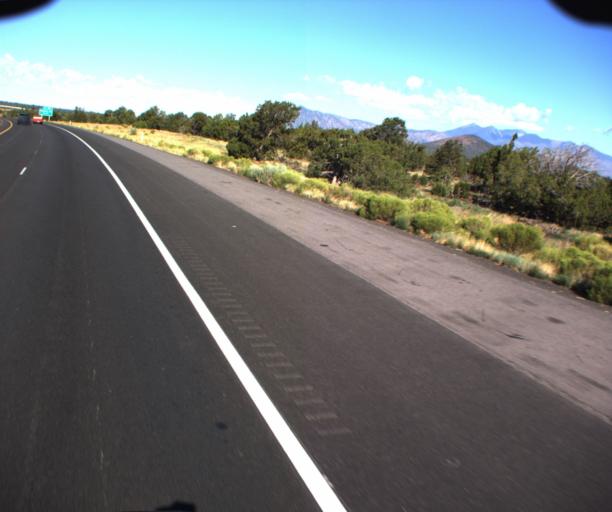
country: US
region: Arizona
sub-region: Coconino County
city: Flagstaff
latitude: 35.2029
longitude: -111.4661
